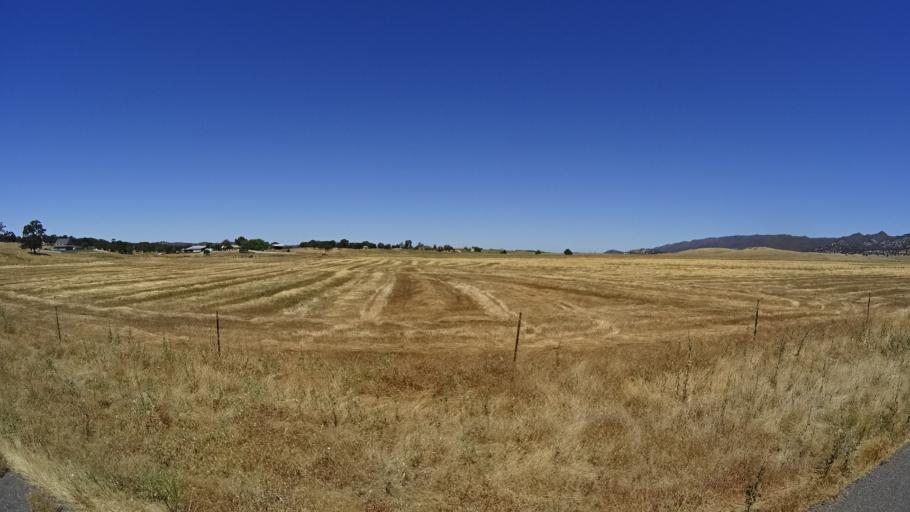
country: US
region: California
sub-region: Calaveras County
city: Copperopolis
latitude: 38.0306
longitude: -120.7141
